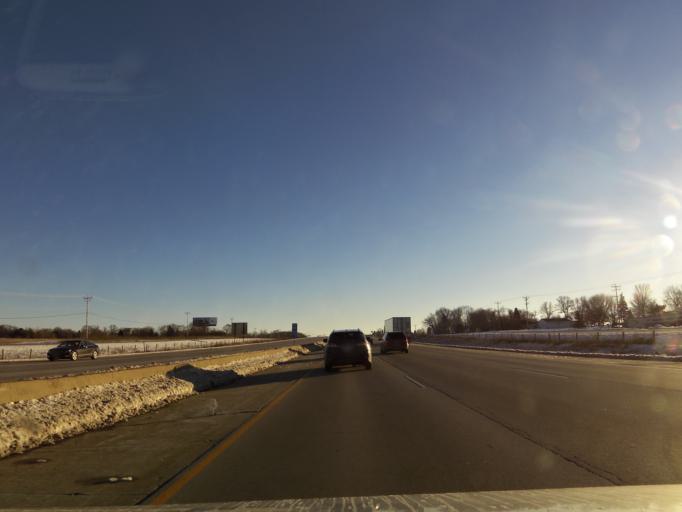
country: US
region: Wisconsin
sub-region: Racine County
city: Franksville
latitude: 42.7687
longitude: -87.9540
